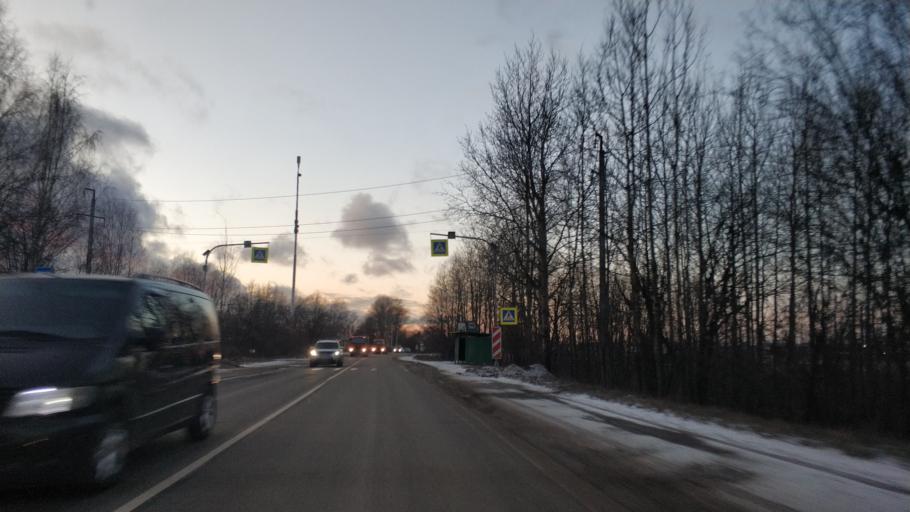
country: RU
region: St.-Petersburg
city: Pontonnyy
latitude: 59.8068
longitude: 30.6208
